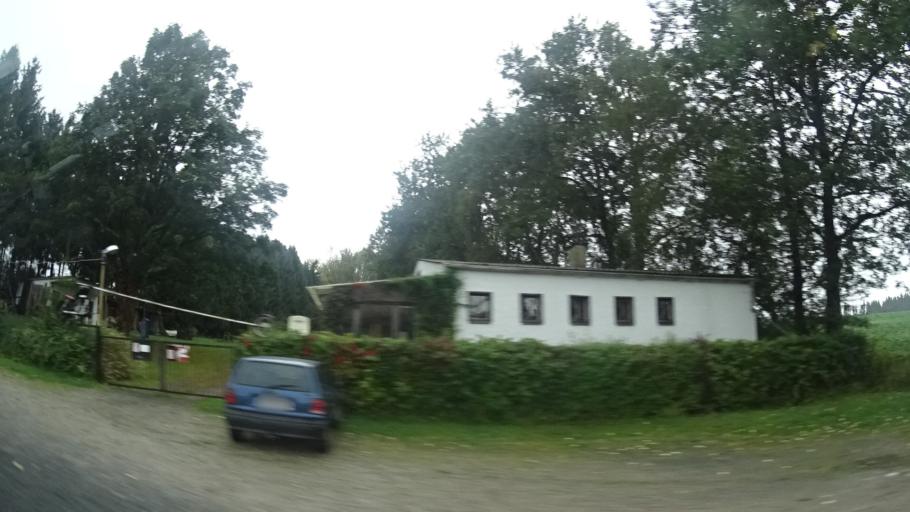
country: DE
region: Thuringia
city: Drognitz
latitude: 50.5355
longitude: 11.5788
